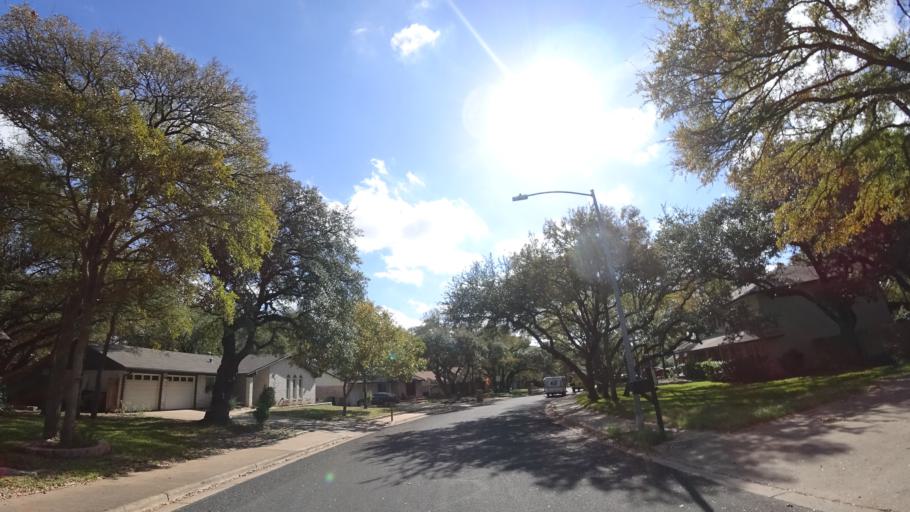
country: US
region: Texas
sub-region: Williamson County
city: Jollyville
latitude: 30.4150
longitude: -97.7271
